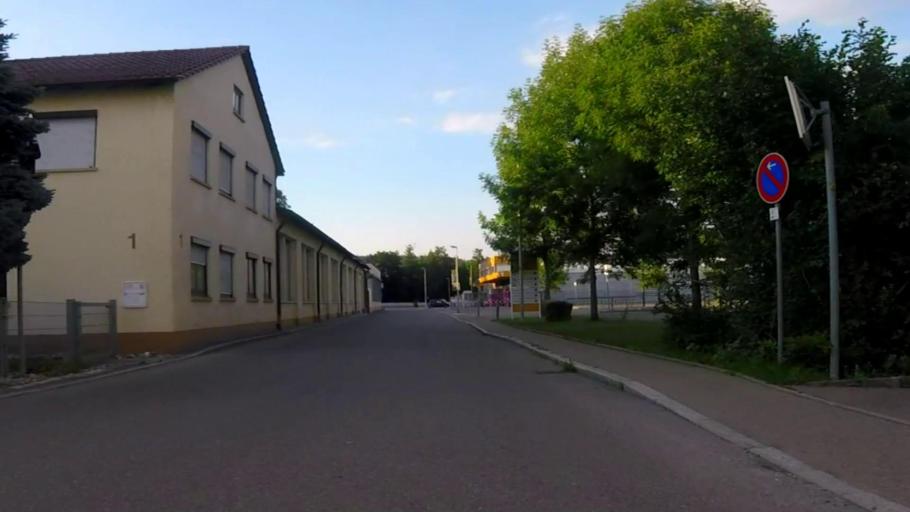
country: DE
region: Baden-Wuerttemberg
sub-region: Regierungsbezirk Stuttgart
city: Oppenweiler
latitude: 48.9822
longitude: 9.4615
